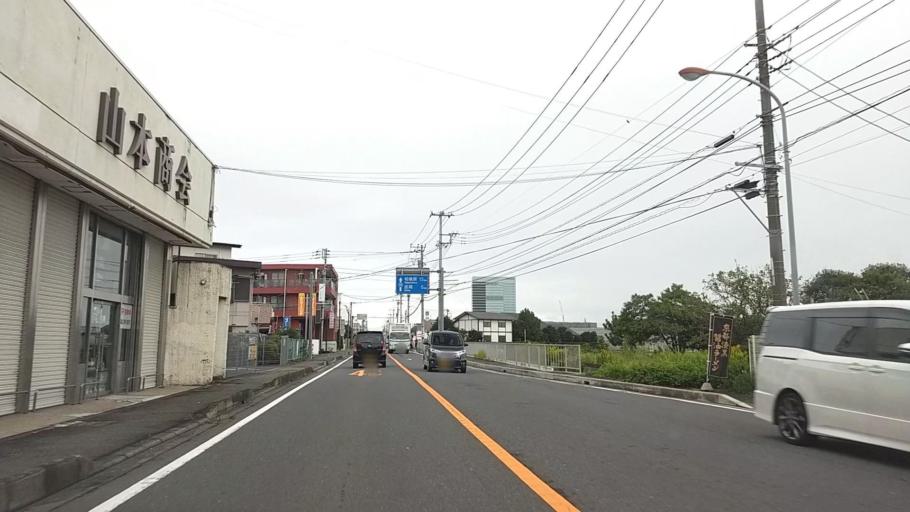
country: JP
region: Kanagawa
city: Atsugi
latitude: 35.4512
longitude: 139.3805
